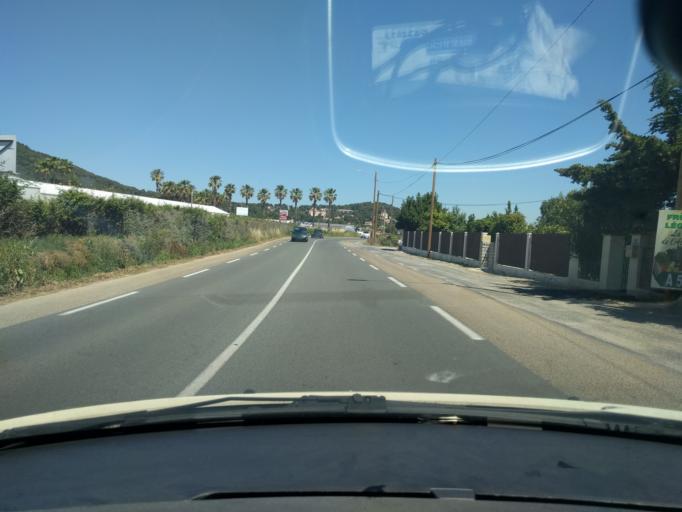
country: FR
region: Provence-Alpes-Cote d'Azur
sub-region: Departement du Var
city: Hyeres
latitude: 43.0841
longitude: 6.1289
